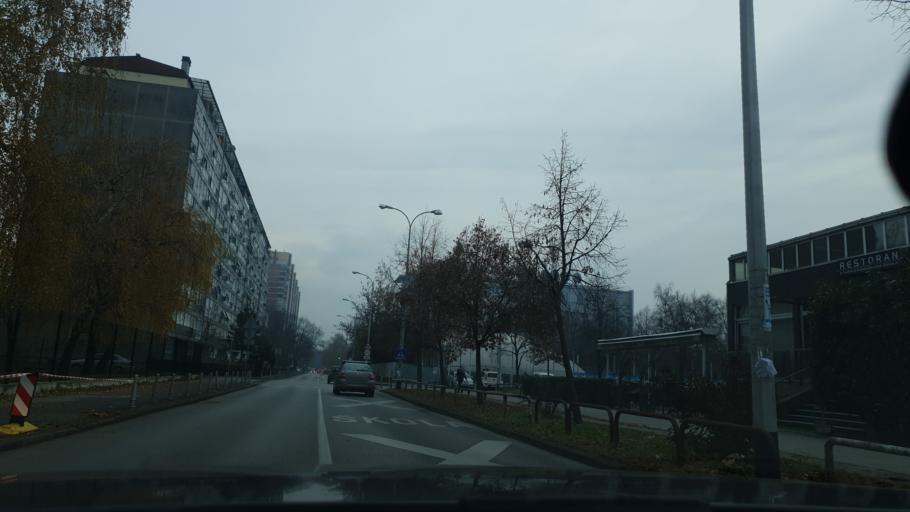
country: HR
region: Grad Zagreb
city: Novi Zagreb
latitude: 45.7752
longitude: 15.9939
